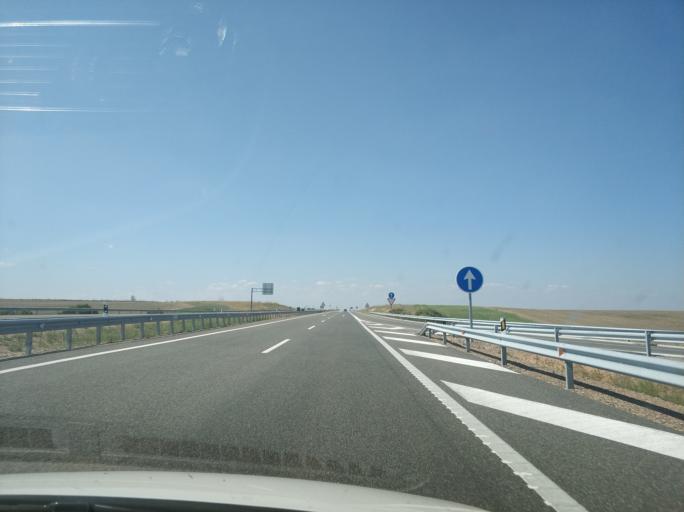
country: ES
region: Castille and Leon
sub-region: Provincia de Zamora
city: Roales
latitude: 41.5800
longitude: -5.7754
